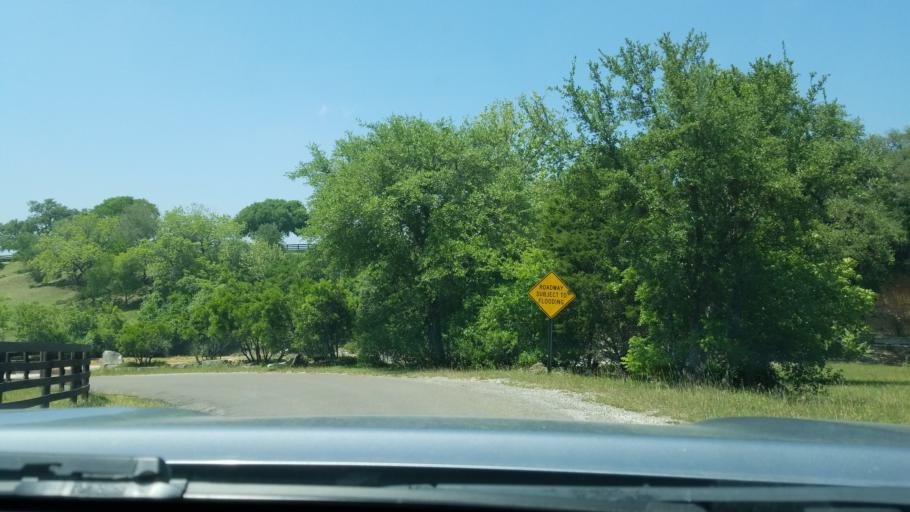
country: US
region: Texas
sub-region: Blanco County
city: Blanco
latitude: 30.0052
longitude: -98.4322
